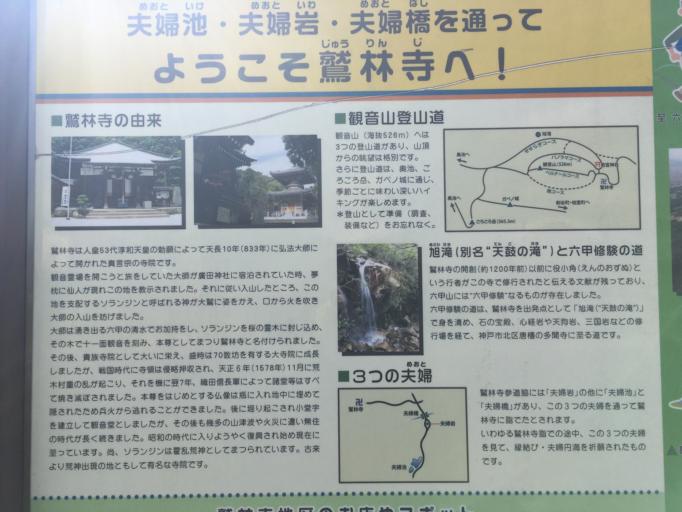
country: JP
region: Hyogo
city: Ashiya
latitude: 34.7741
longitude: 135.3160
